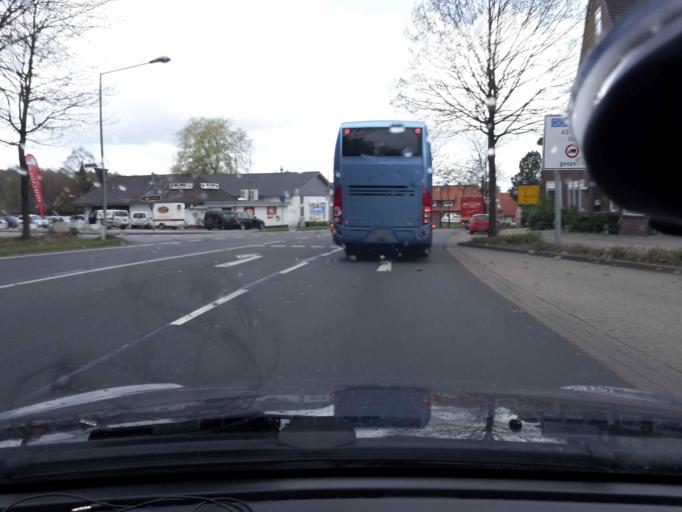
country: DE
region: Lower Saxony
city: Nottensdorf
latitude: 53.4793
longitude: 9.6372
